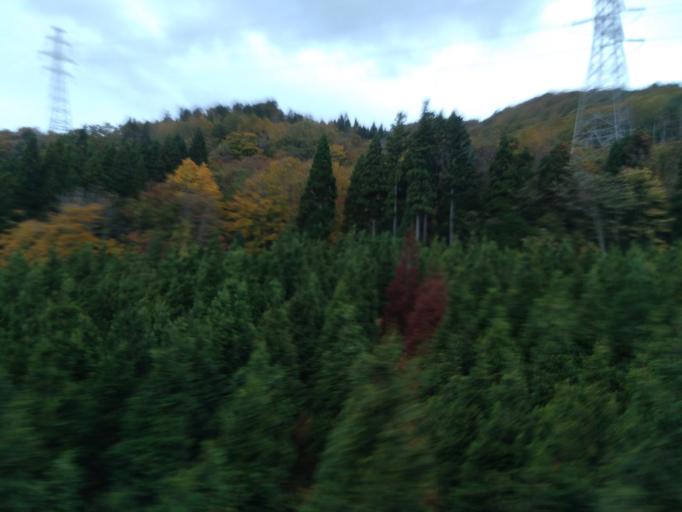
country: JP
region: Aomori
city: Goshogawara
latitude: 41.1519
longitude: 140.5094
